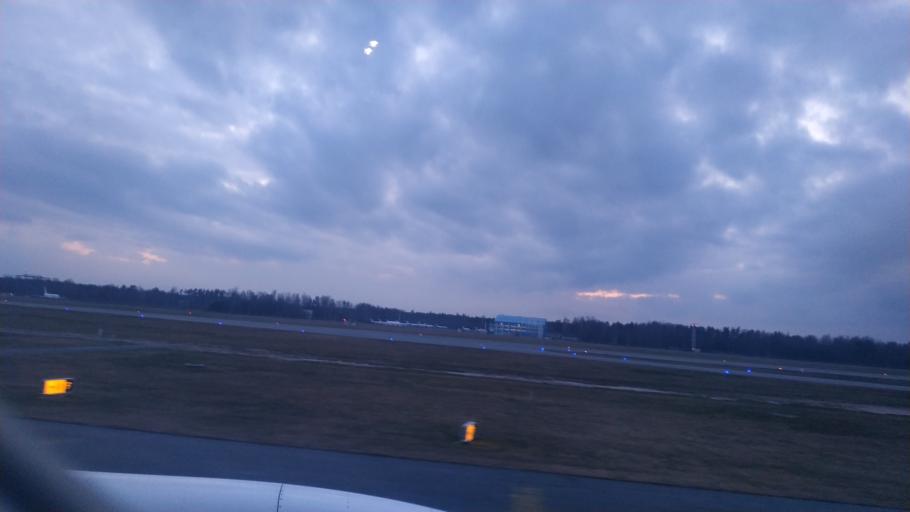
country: LV
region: Babite
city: Pinki
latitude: 56.9243
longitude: 23.9753
